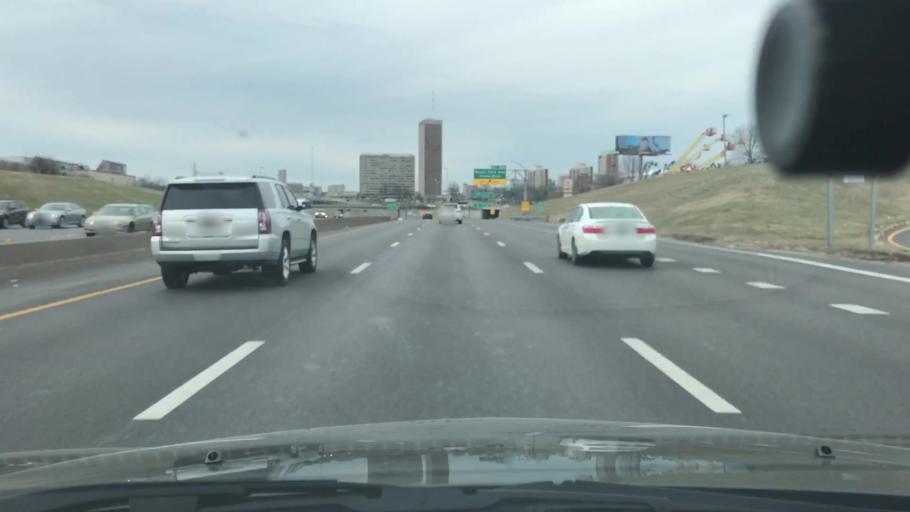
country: US
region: Missouri
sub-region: City of Saint Louis
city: St. Louis
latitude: 38.6293
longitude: -90.2228
